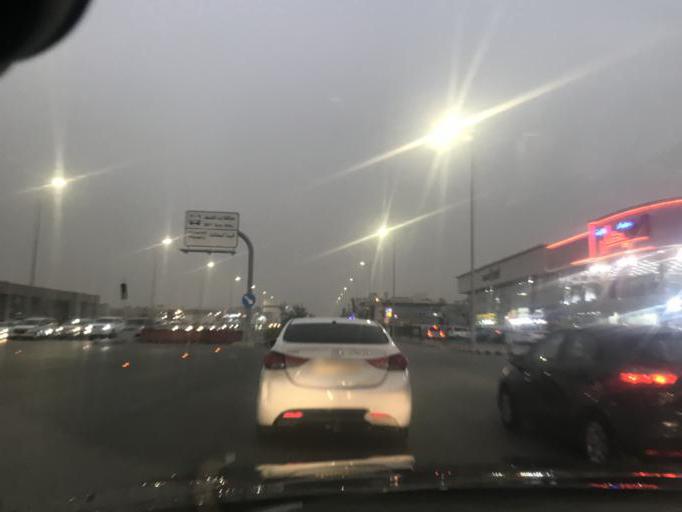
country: SA
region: Ar Riyad
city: Riyadh
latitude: 24.7423
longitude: 46.7827
